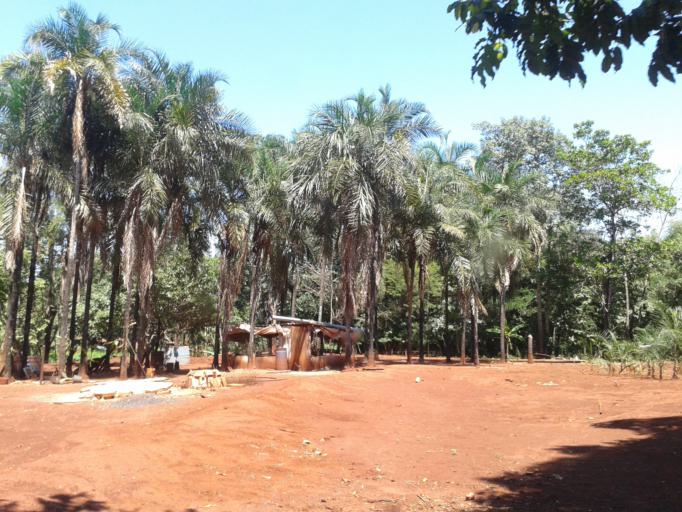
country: BR
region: Minas Gerais
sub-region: Centralina
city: Centralina
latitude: -18.6281
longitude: -49.2956
